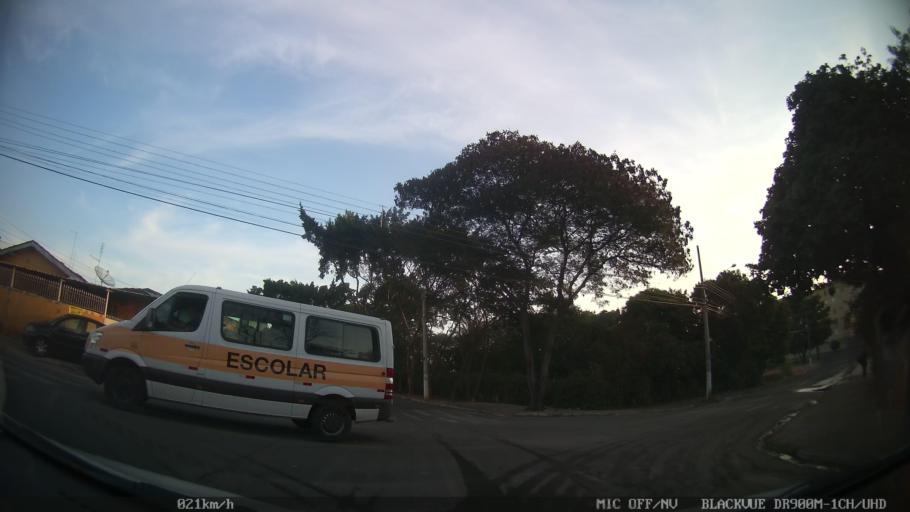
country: BR
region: Sao Paulo
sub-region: Campinas
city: Campinas
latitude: -22.9770
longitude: -47.1404
